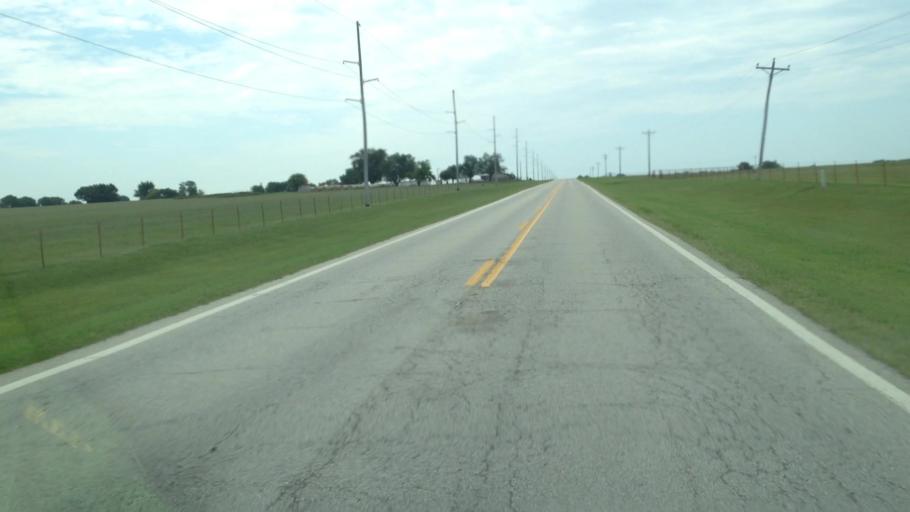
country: US
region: Kansas
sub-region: Labette County
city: Chetopa
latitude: 36.9123
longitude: -95.0897
